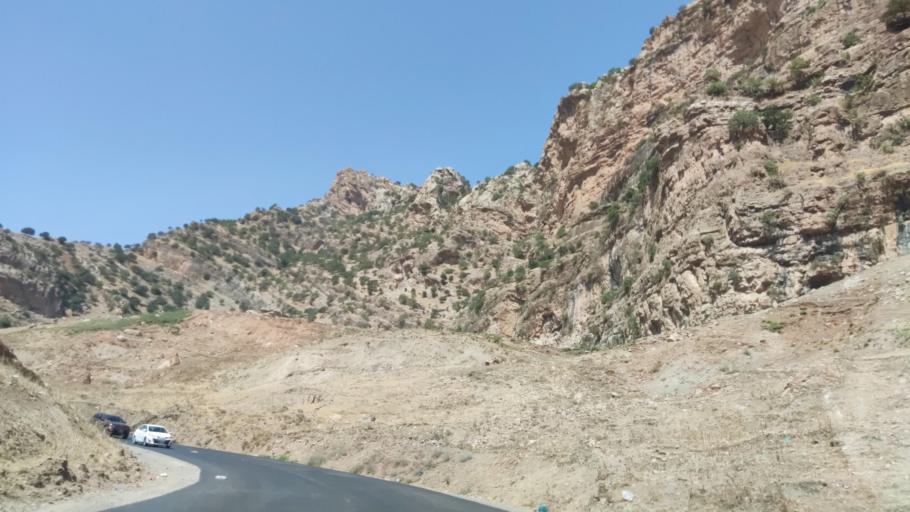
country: IQ
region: Arbil
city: Ruwandiz
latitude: 36.6330
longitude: 44.4457
